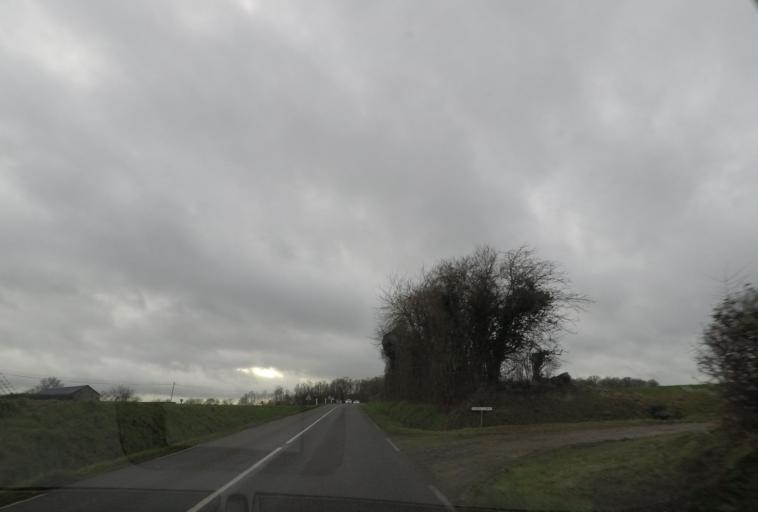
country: FR
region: Pays de la Loire
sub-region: Departement de la Sarthe
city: Vibraye
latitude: 47.9897
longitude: 0.7628
